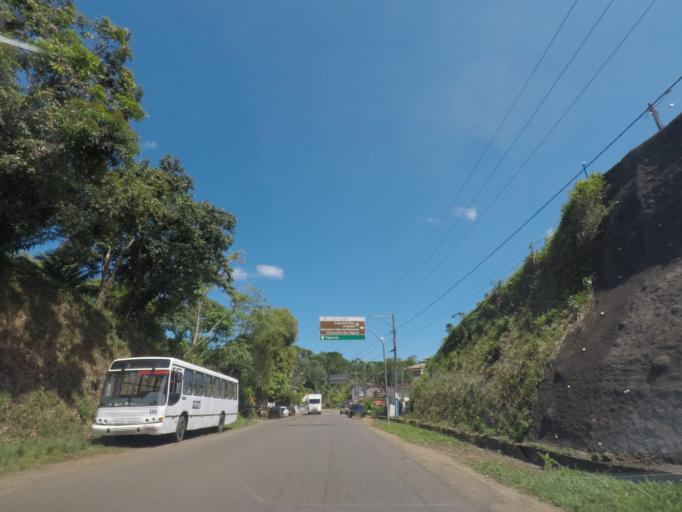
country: BR
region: Bahia
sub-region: Taperoa
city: Taperoa
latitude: -13.5013
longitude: -39.0962
